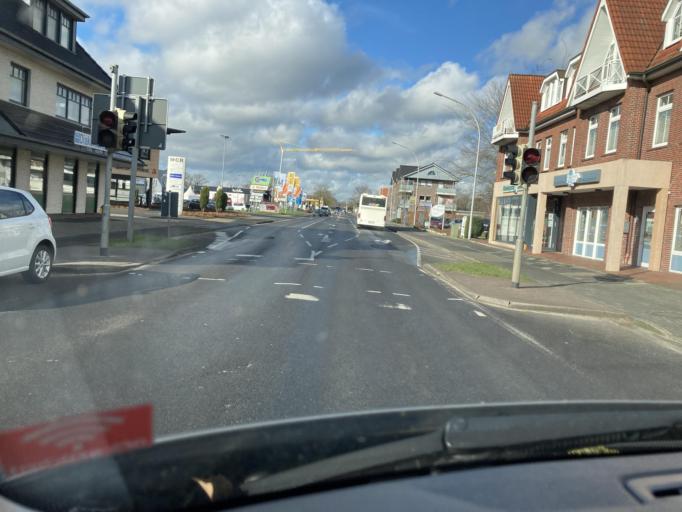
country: DE
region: Lower Saxony
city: Ostrhauderfehn
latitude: 53.1367
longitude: 7.5739
